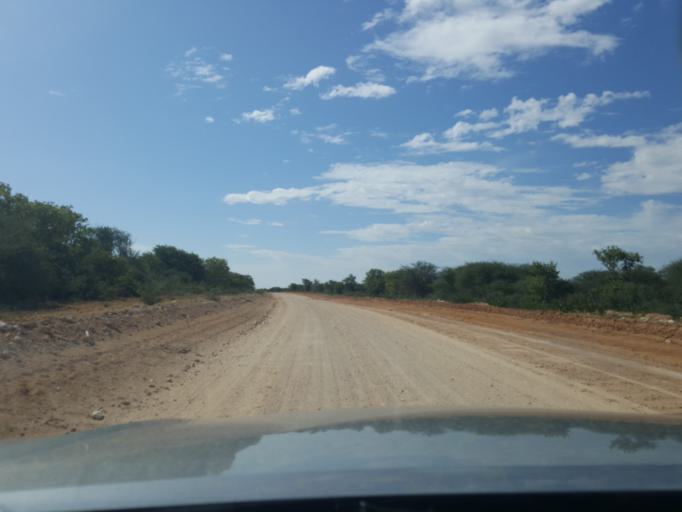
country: BW
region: Kweneng
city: Khudumelapye
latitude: -23.7719
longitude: 24.7671
